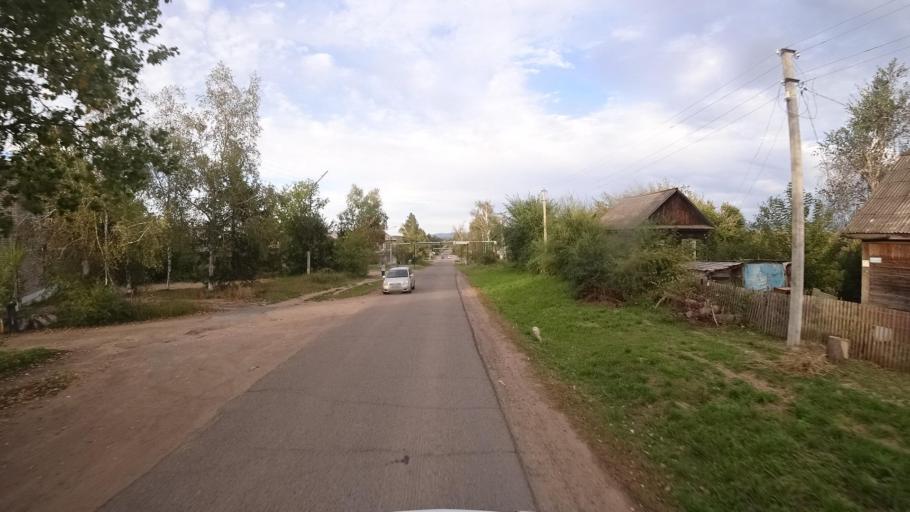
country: RU
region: Primorskiy
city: Yakovlevka
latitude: 44.4257
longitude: 133.4785
